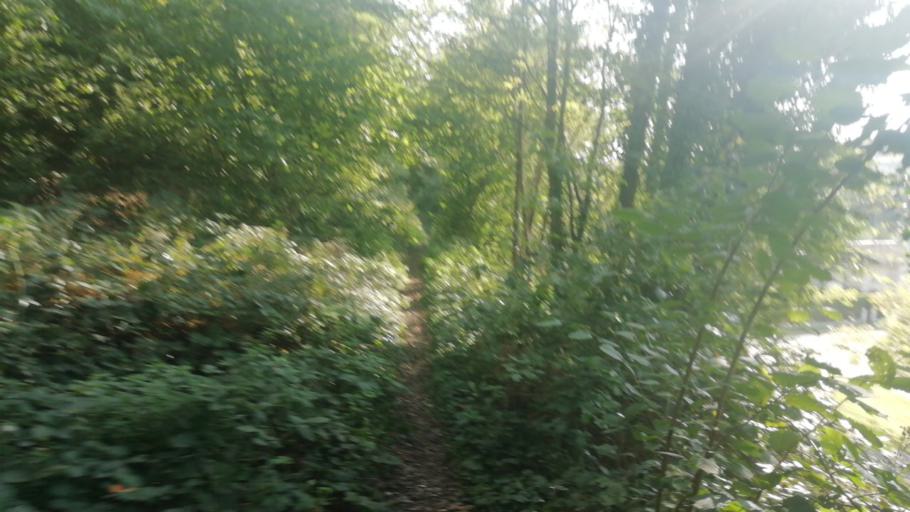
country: FR
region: Haute-Normandie
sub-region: Departement de la Seine-Maritime
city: Rolleville
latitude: 49.5907
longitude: 0.2124
